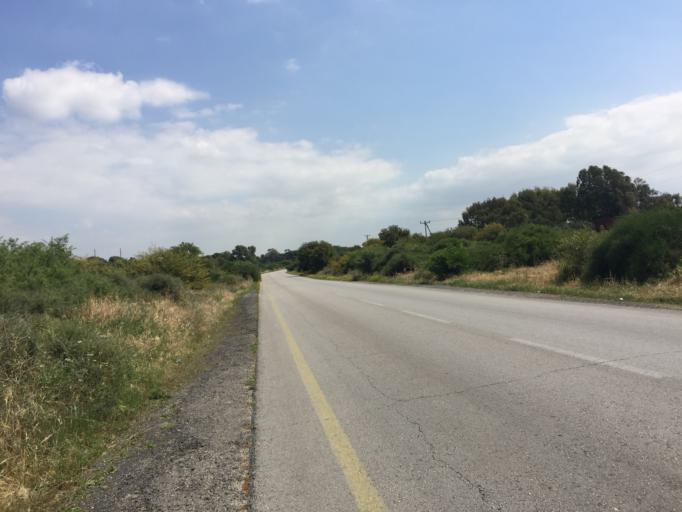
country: IL
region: Haifa
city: Qesarya
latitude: 32.4958
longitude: 34.8947
